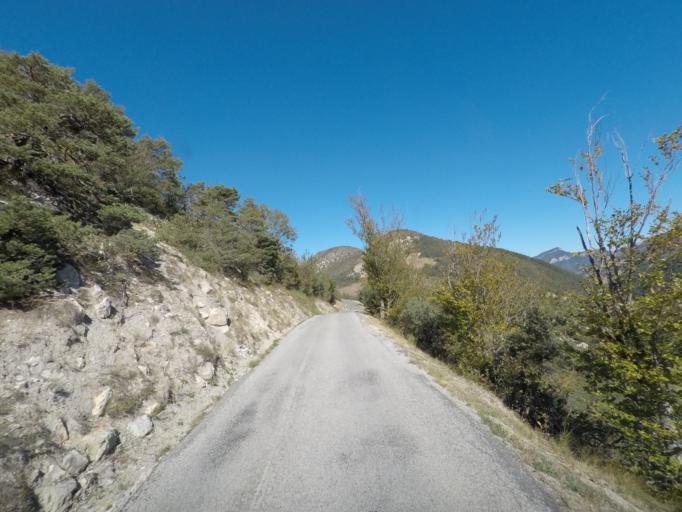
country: FR
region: Rhone-Alpes
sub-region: Departement de la Drome
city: Die
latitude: 44.5703
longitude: 5.3049
